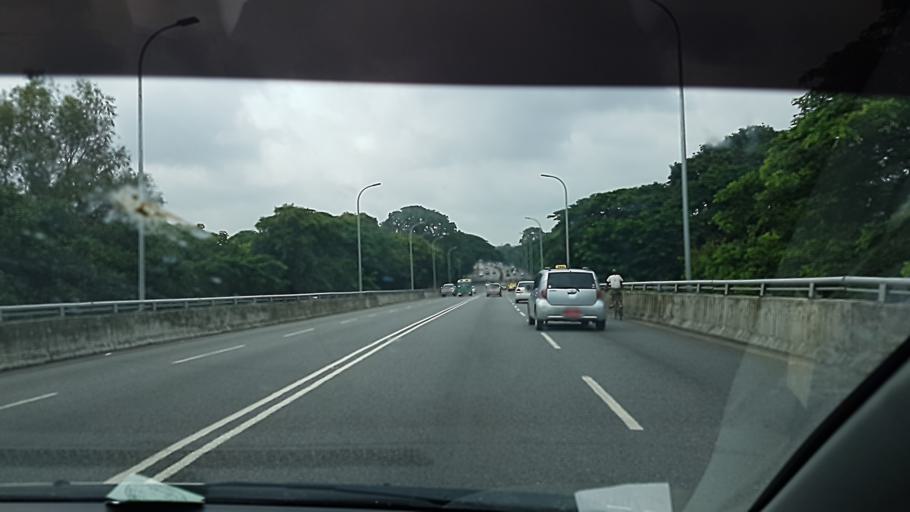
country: MM
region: Yangon
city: Yangon
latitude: 16.8012
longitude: 96.1380
